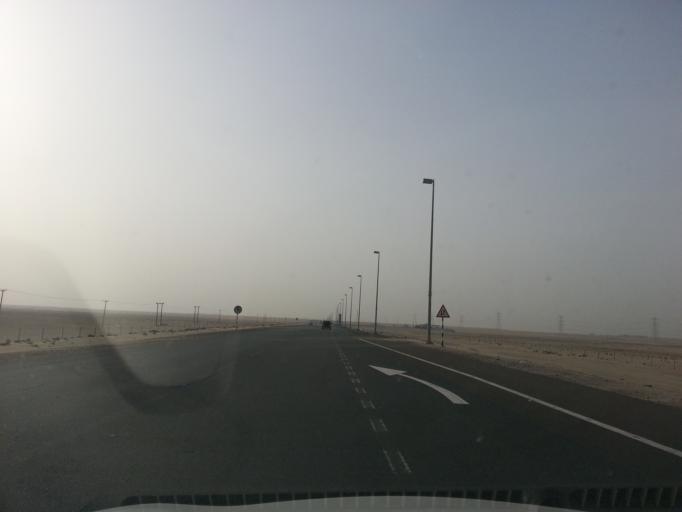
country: AE
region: Dubai
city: Dubai
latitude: 24.7964
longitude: 55.0742
